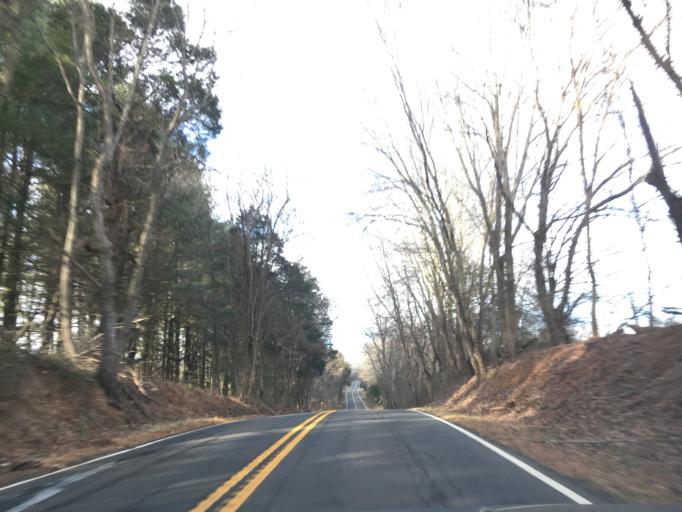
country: US
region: Virginia
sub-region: Fauquier County
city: Marshall
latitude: 38.7376
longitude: -77.9564
